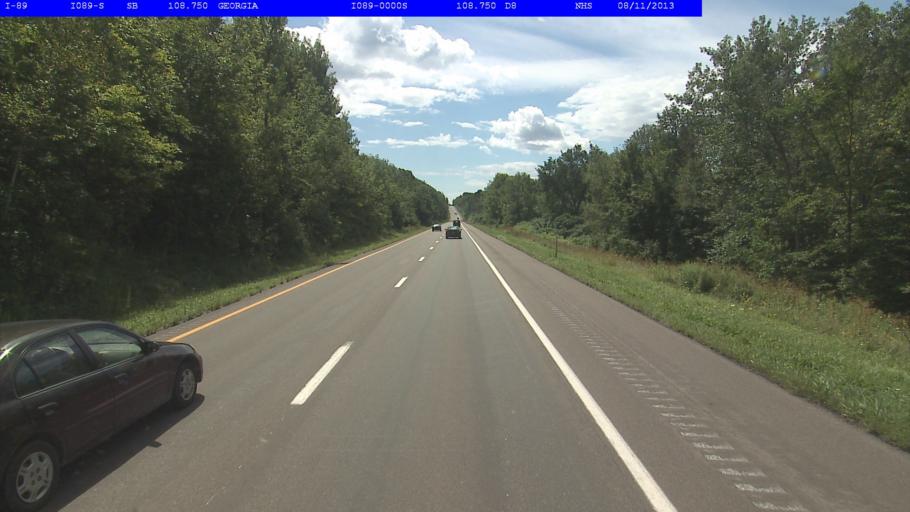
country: US
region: Vermont
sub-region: Franklin County
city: Saint Albans
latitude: 44.7236
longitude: -73.0831
